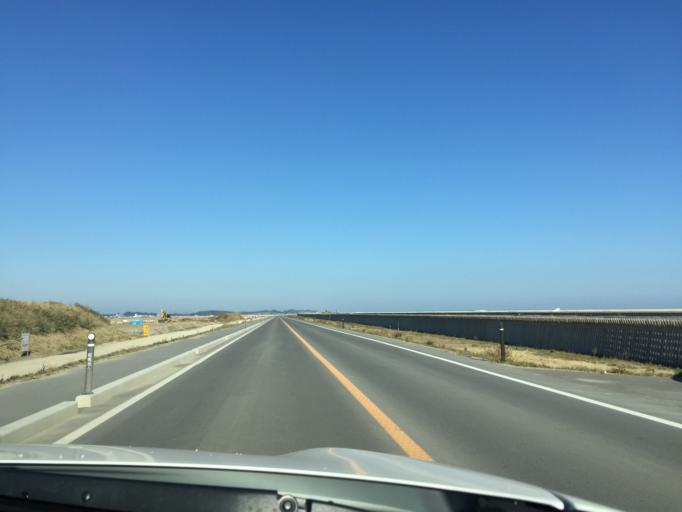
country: JP
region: Miyagi
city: Marumori
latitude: 37.7836
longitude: 140.9842
